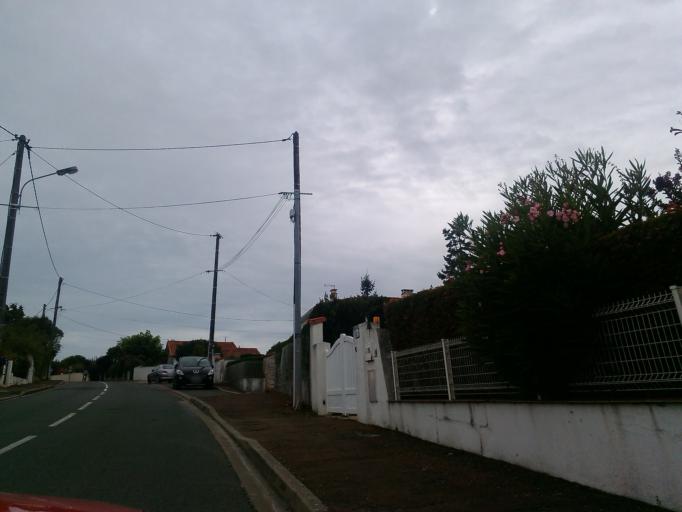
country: FR
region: Poitou-Charentes
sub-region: Departement de la Charente-Maritime
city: Vaux-sur-Mer
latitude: 45.6413
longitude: -1.0670
